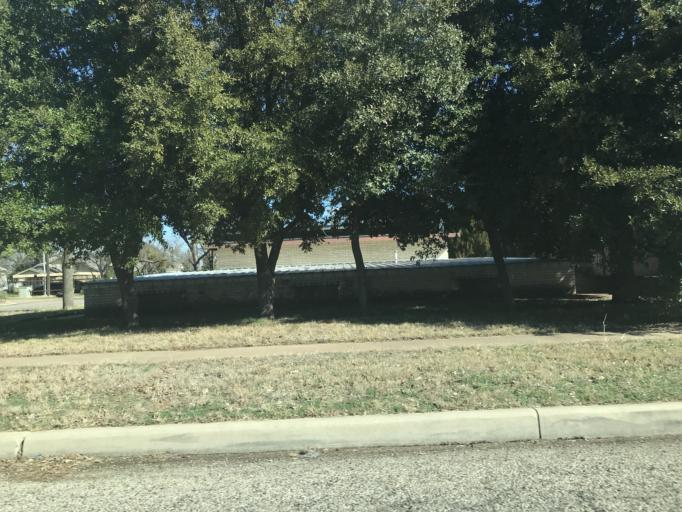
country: US
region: Texas
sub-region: Tom Green County
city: San Angelo
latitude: 31.4484
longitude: -100.4447
